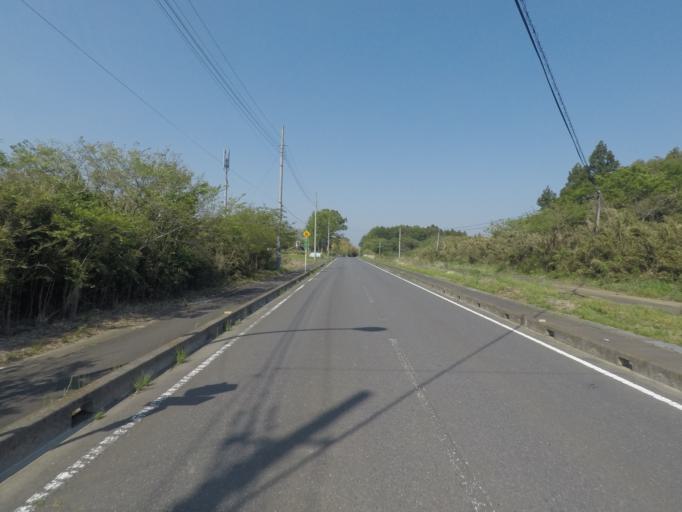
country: JP
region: Ibaraki
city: Inashiki
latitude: 36.0759
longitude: 140.3739
